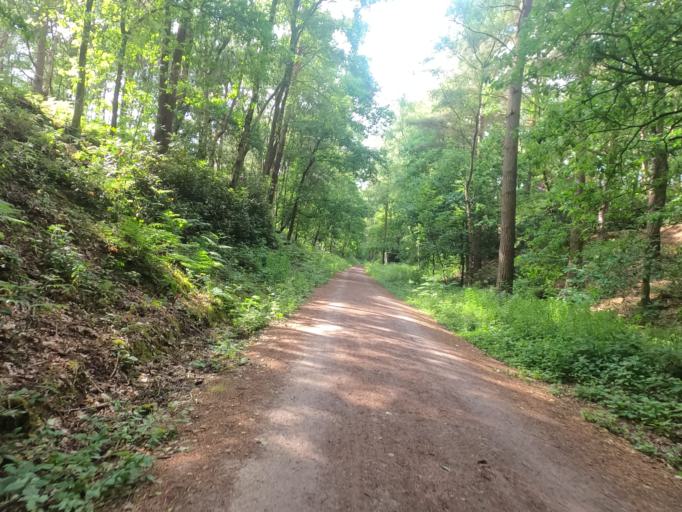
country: GB
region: England
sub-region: Cheshire West and Chester
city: Cuddington
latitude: 53.2187
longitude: -2.6102
